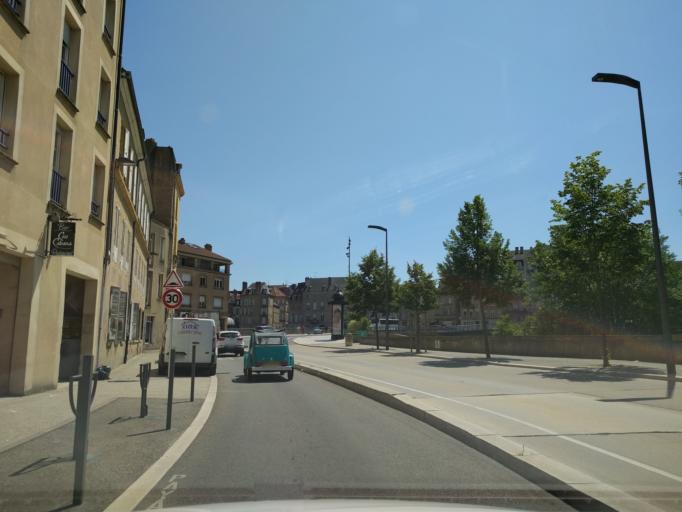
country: FR
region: Lorraine
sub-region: Departement de la Moselle
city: Metz
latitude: 49.1199
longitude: 6.1692
